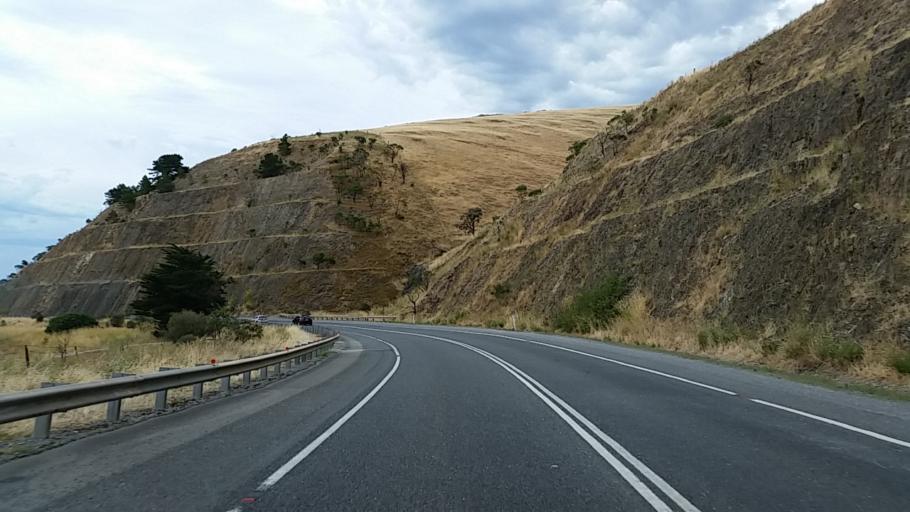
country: AU
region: South Australia
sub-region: Onkaparinga
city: Aldinga
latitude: -35.3649
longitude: 138.4561
